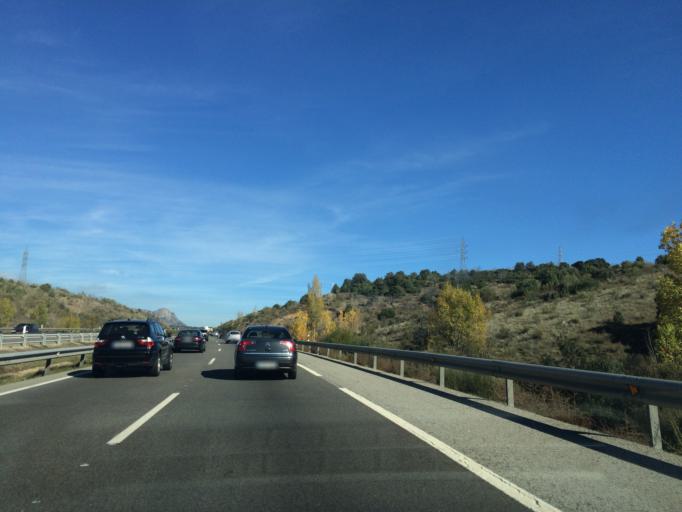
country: ES
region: Madrid
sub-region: Provincia de Madrid
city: Cabanillas de la Sierra
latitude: 40.8129
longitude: -3.6167
